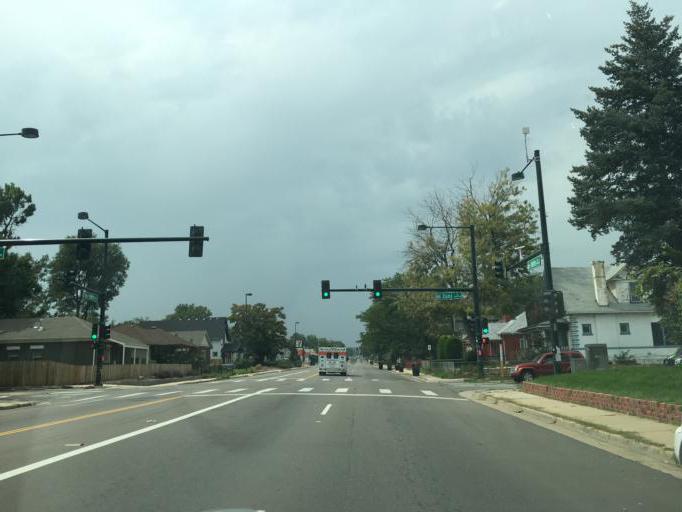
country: US
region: Colorado
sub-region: Adams County
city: Berkley
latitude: 39.7693
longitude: -105.0153
